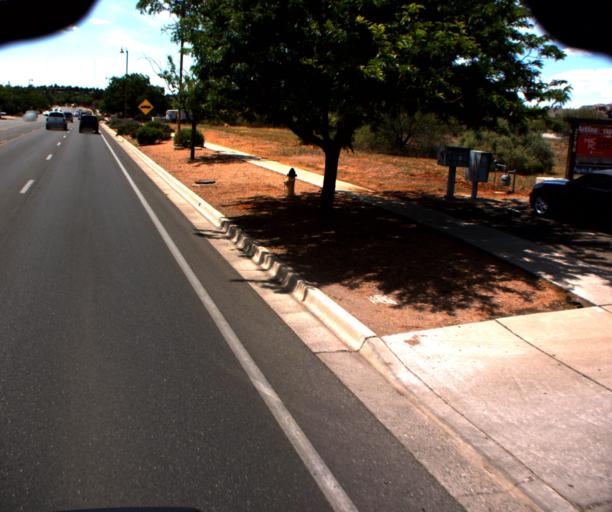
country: US
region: Arizona
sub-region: Yavapai County
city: West Sedona
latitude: 34.8625
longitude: -111.8085
